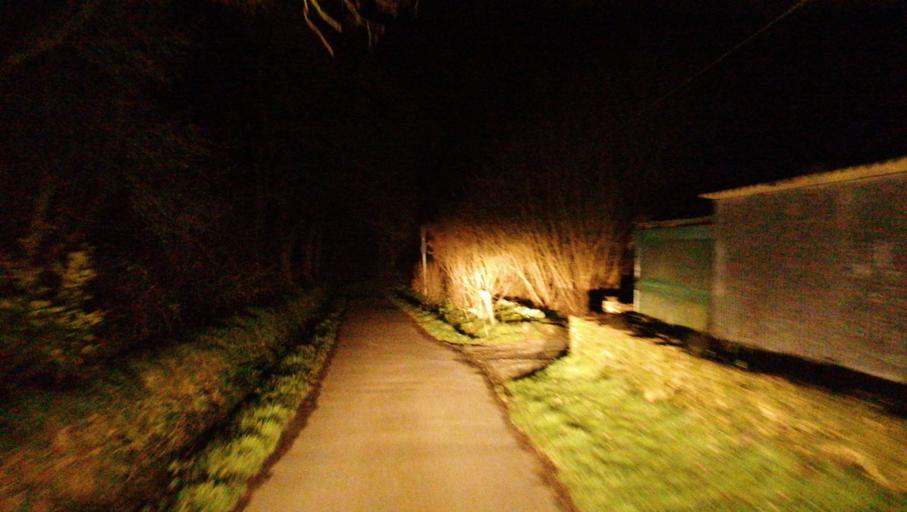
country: FR
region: Brittany
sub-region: Departement des Cotes-d'Armor
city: Saint-Agathon
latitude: 48.5720
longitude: -3.0719
